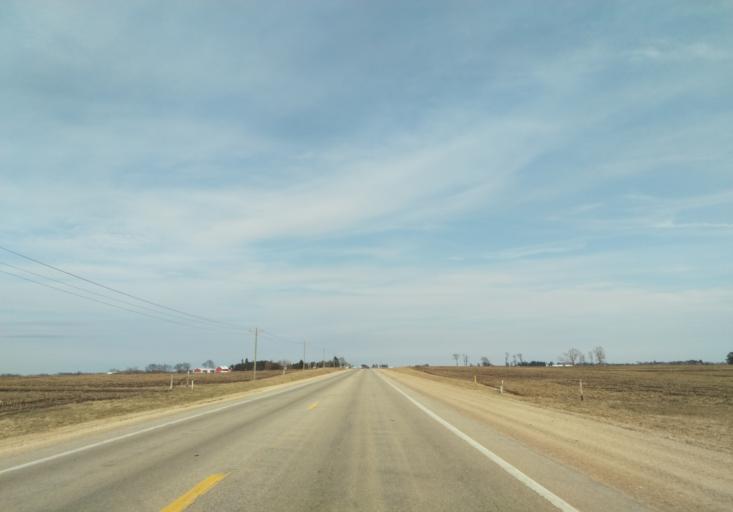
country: US
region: Wisconsin
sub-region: Grant County
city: Lancaster
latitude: 42.9683
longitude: -90.8893
